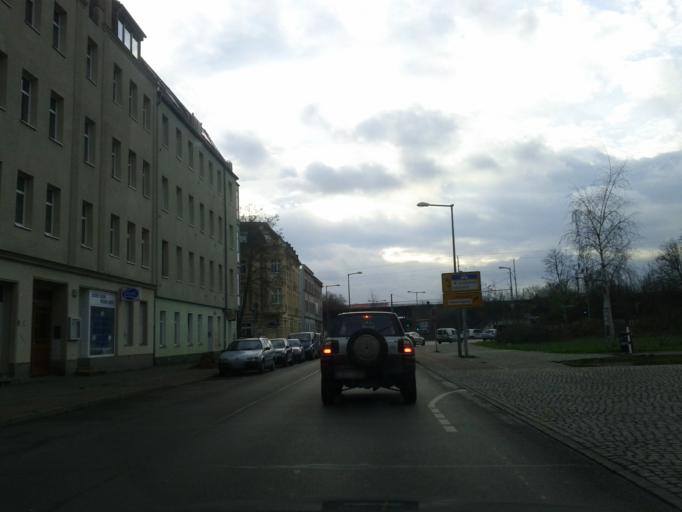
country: DE
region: Berlin
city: Kopenick Bezirk
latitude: 52.4378
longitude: 13.5634
